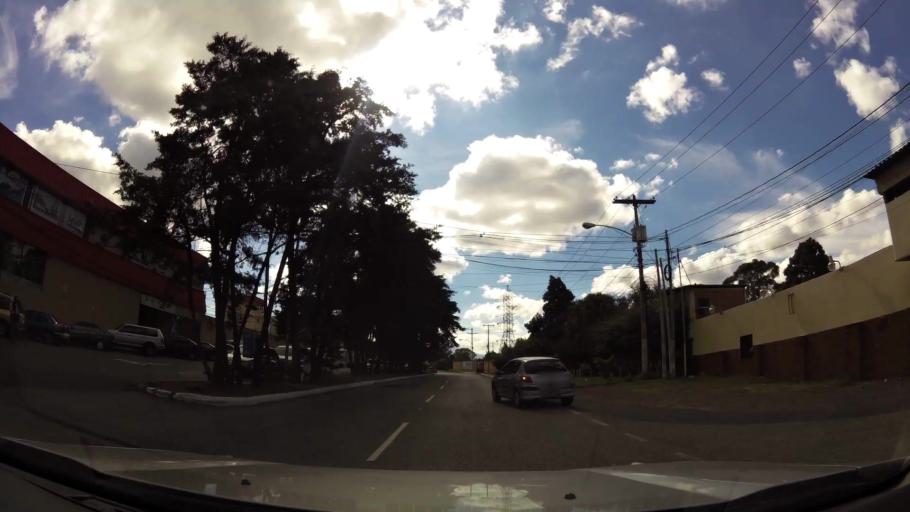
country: GT
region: Guatemala
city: Mixco
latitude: 14.6028
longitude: -90.5621
